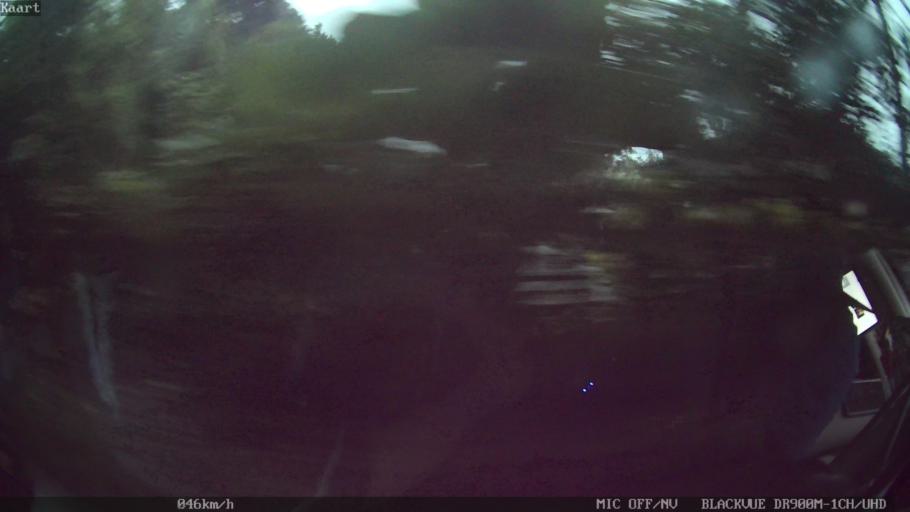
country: ID
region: Bali
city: Banjar Taro Kelod
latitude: -8.3555
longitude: 115.2765
